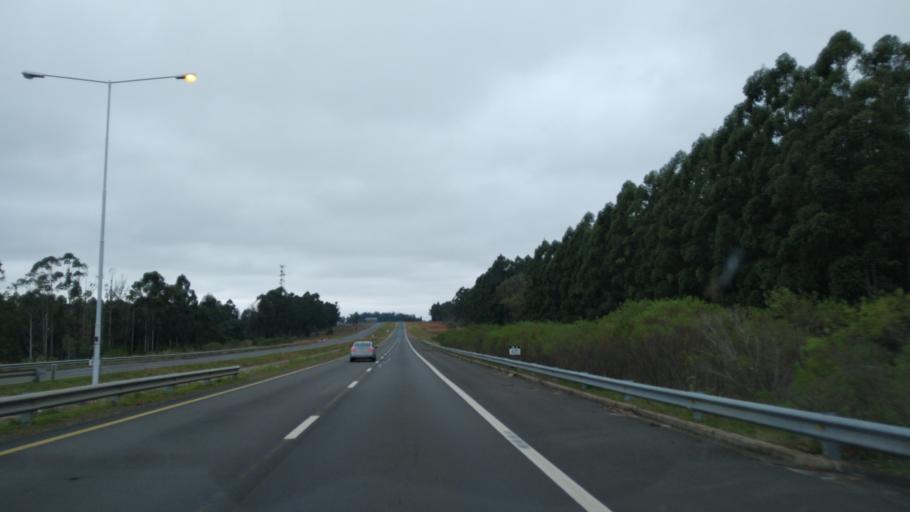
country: AR
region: Corrientes
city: Libertad
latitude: -30.0575
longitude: -57.8094
